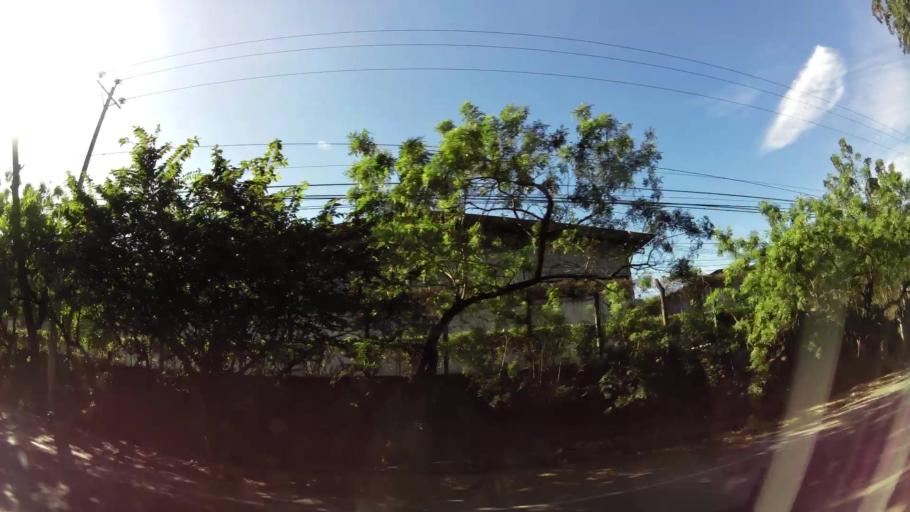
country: SV
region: Santa Ana
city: Santa Ana
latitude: 14.0078
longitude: -89.5464
